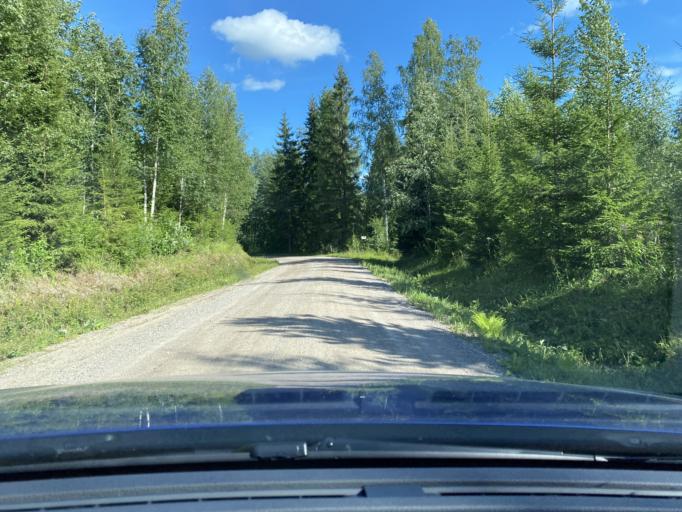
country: FI
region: Pirkanmaa
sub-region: Ylae-Pirkanmaa
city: Maenttae
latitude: 62.0179
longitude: 24.7480
